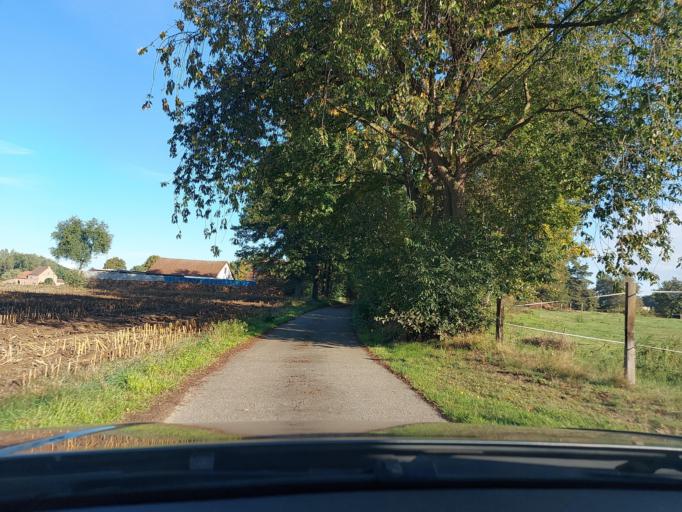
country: BE
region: Flanders
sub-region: Provincie Antwerpen
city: Meerhout
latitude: 51.1118
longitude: 5.0444
